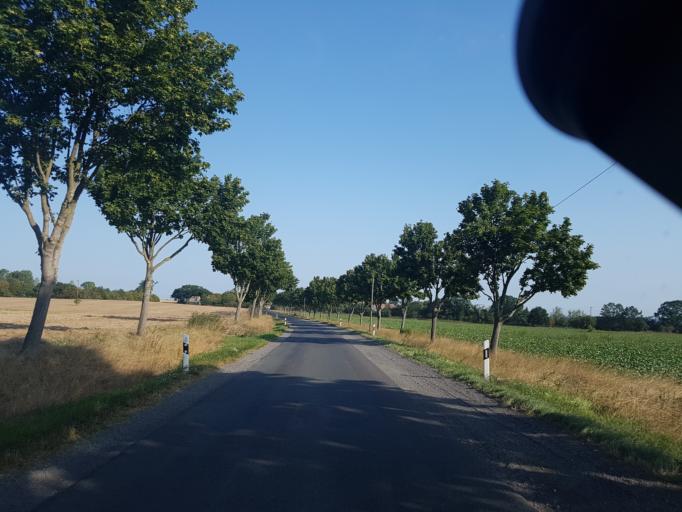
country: DE
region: Brandenburg
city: Niemegk
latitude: 52.0217
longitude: 12.6838
